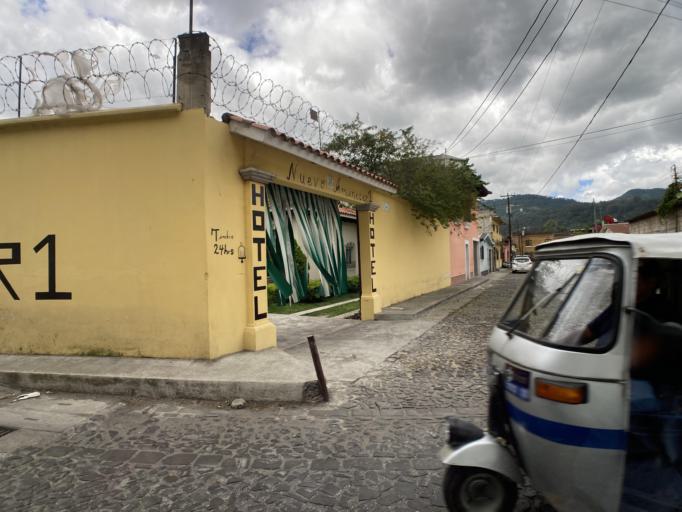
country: GT
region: Sacatepequez
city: Jocotenango
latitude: 14.5700
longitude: -90.7431
